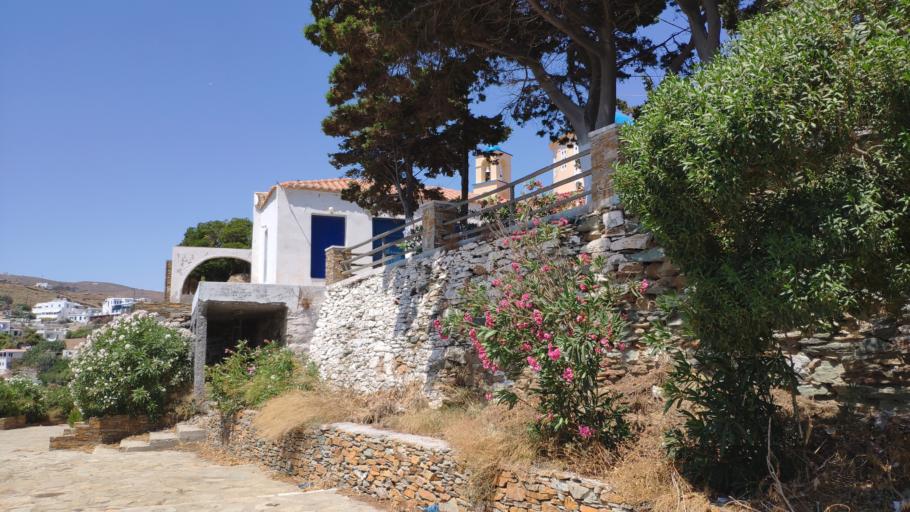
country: GR
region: South Aegean
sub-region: Nomos Kykladon
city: Kythnos
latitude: 37.3444
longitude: 24.4360
